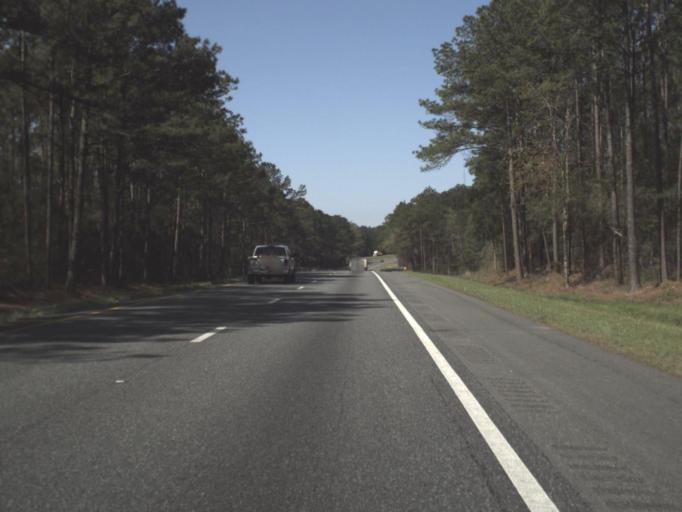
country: US
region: Florida
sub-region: Walton County
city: DeFuniak Springs
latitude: 30.6916
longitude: -86.0202
